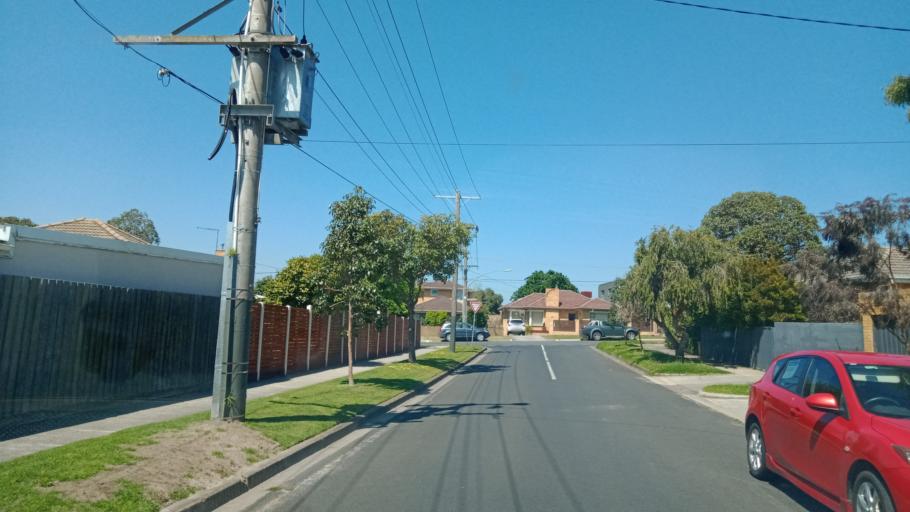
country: AU
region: Victoria
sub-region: Monash
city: Oakleigh South
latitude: -37.9172
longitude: 145.0786
